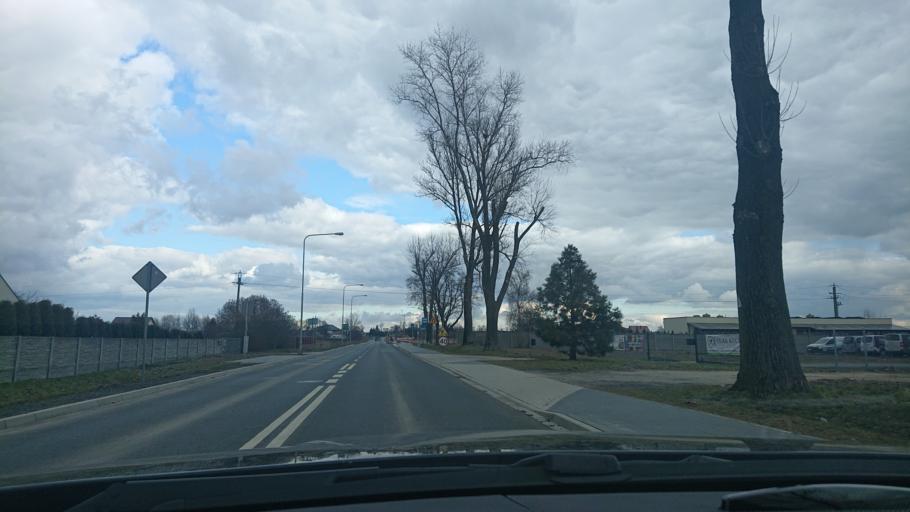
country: PL
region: Greater Poland Voivodeship
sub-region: Powiat gnieznienski
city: Gniezno
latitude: 52.5427
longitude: 17.6528
